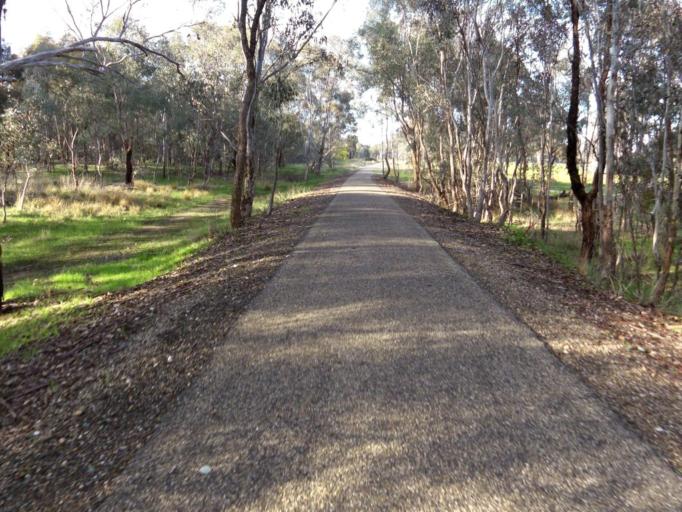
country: AU
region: Victoria
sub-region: Wangaratta
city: Wangaratta
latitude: -36.4111
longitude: 146.5492
